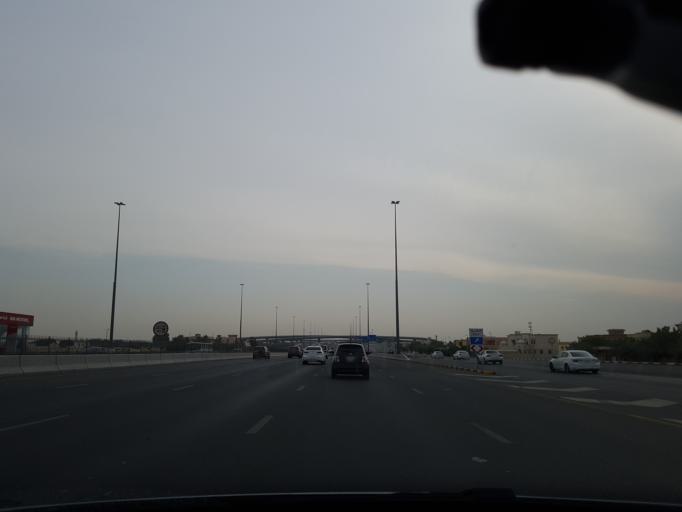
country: AE
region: Ash Shariqah
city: Sharjah
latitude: 25.3424
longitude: 55.4707
